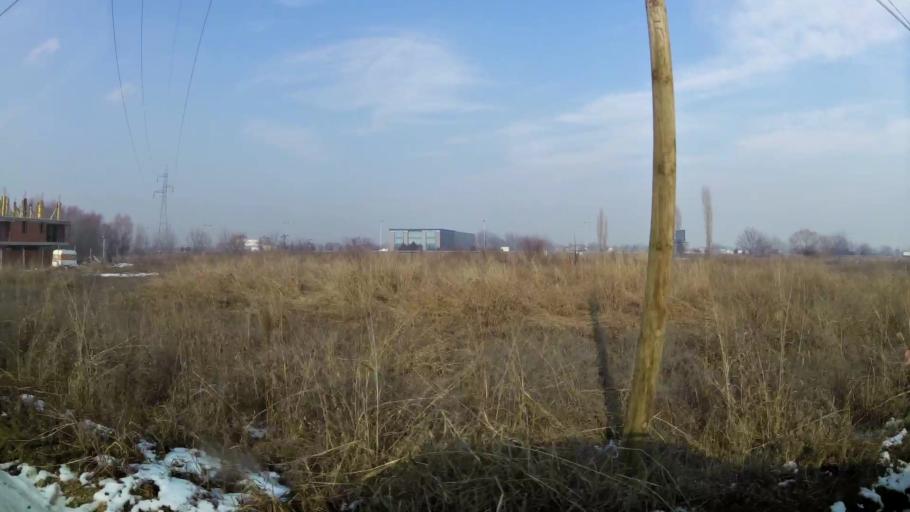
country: MK
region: Kisela Voda
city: Kisela Voda
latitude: 41.9958
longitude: 21.5160
